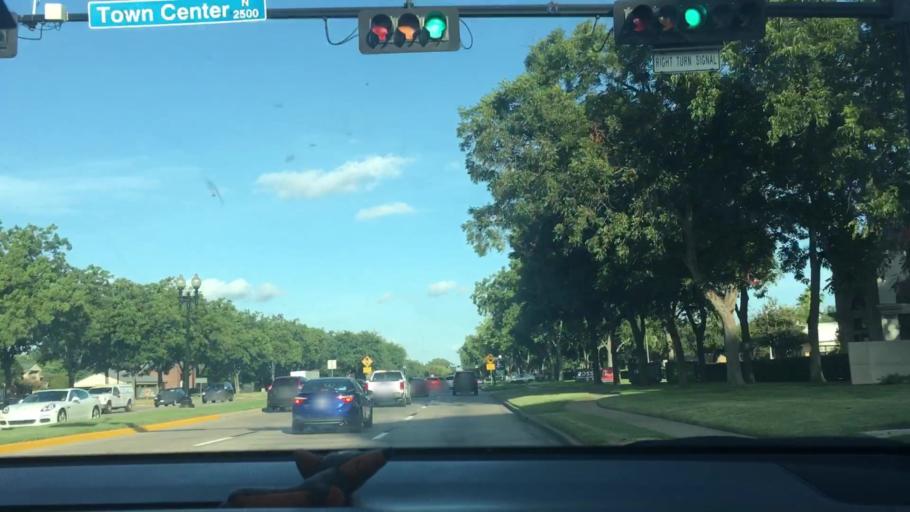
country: US
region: Texas
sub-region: Fort Bend County
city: Sugar Land
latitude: 29.5971
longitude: -95.6192
